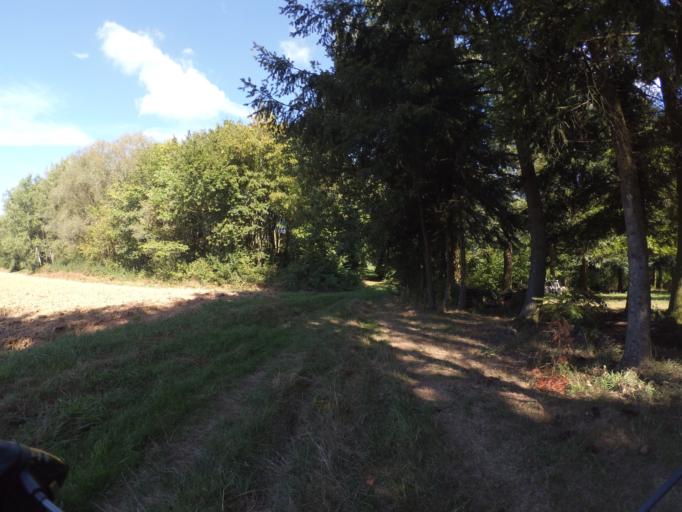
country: DE
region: Rheinland-Pfalz
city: Bekond
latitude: 49.8708
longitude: 6.7888
